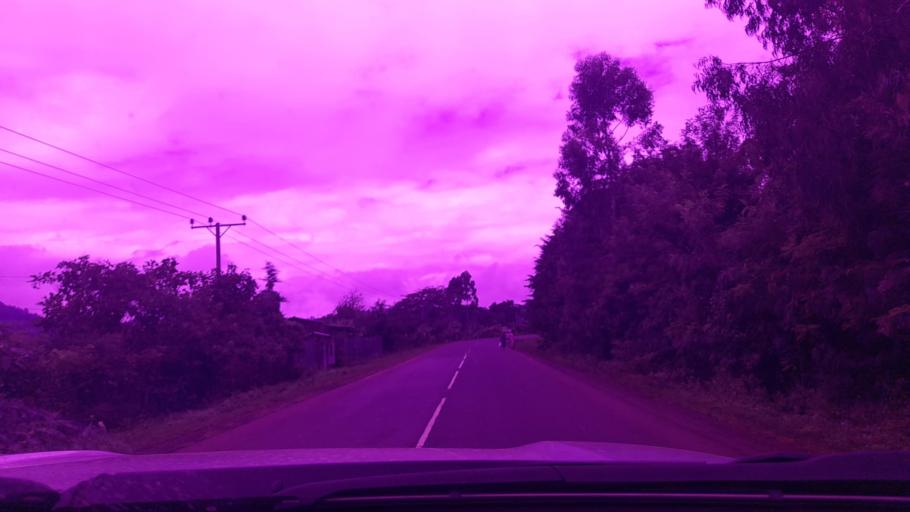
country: ET
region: Oromiya
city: Jima
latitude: 7.5551
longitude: 36.6108
